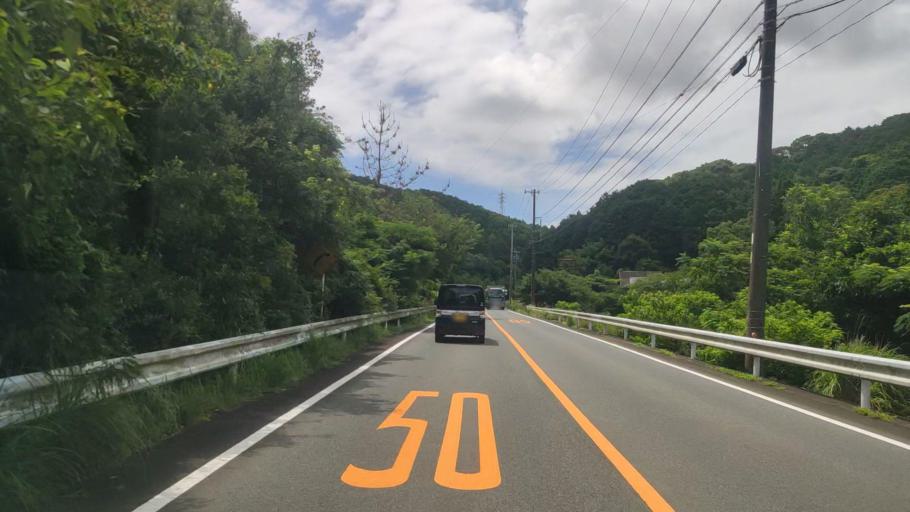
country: JP
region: Mie
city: Toba
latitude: 34.4160
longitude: 136.8162
